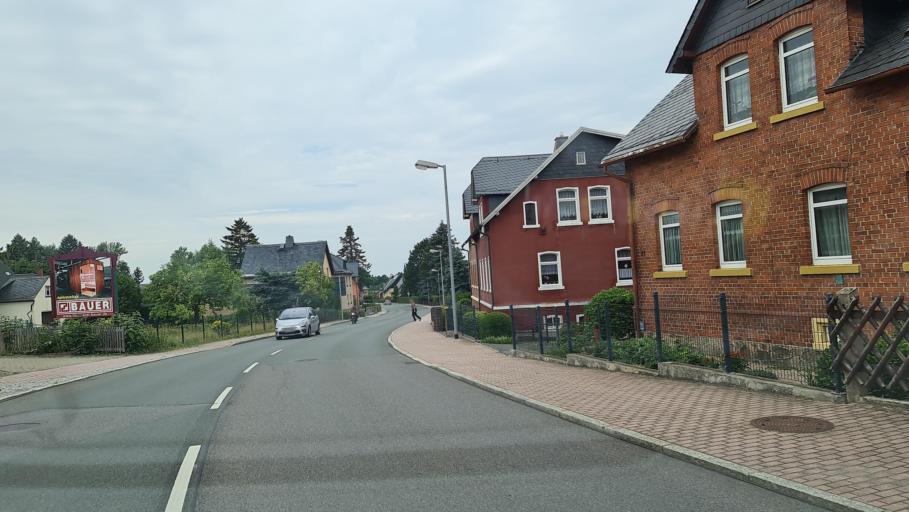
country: DE
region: Saxony
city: Stutzengrun
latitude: 50.5358
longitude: 12.5075
